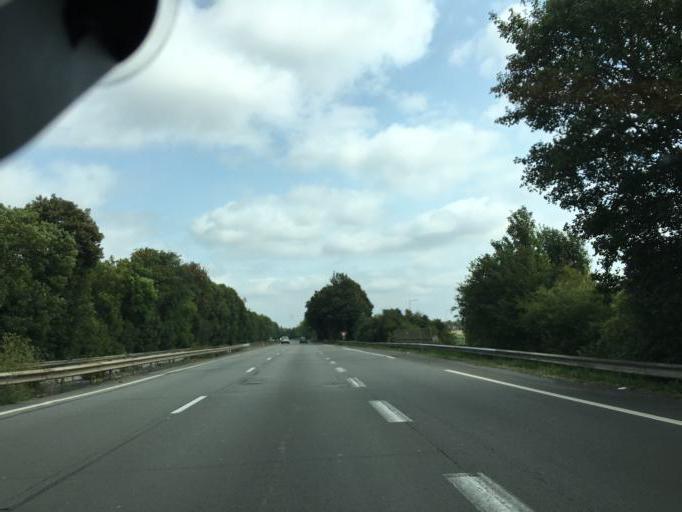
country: FR
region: Nord-Pas-de-Calais
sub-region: Departement du Pas-de-Calais
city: Grenay
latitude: 50.4377
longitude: 2.7548
